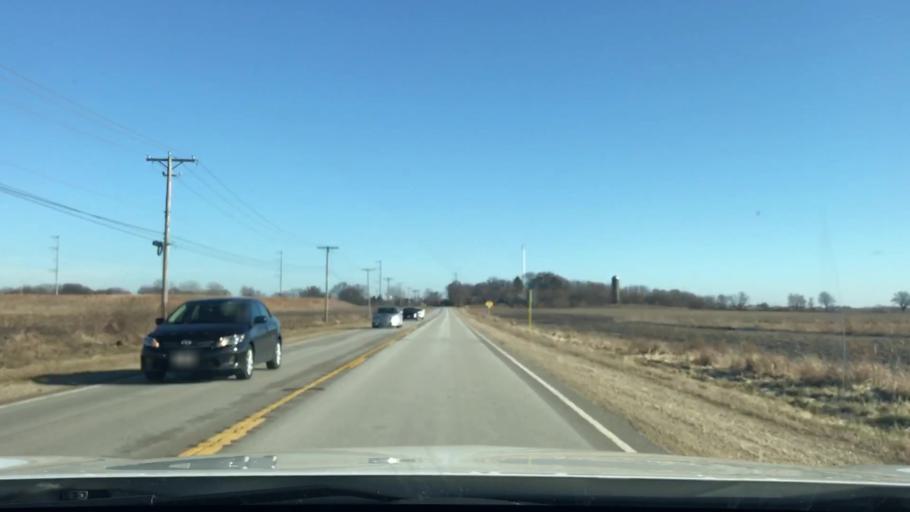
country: US
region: Illinois
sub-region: Kane County
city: Gilberts
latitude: 42.1002
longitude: -88.3912
